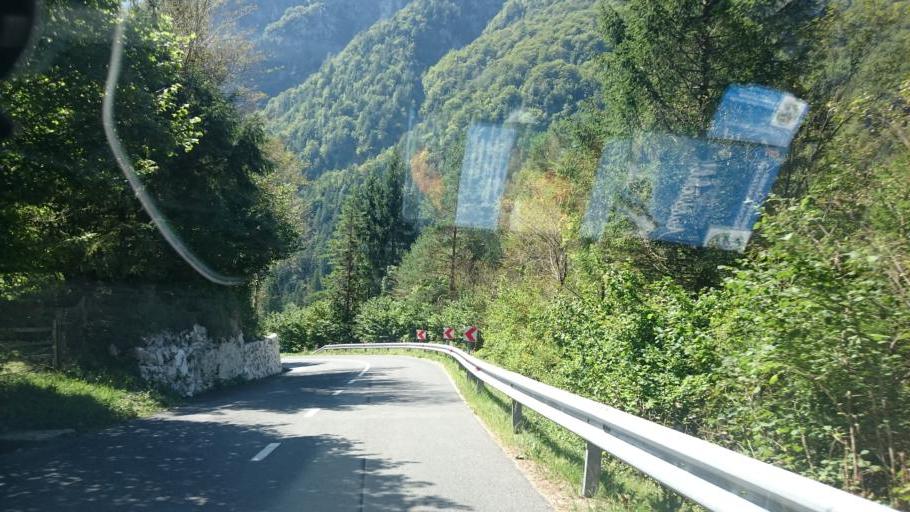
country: SI
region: Bovec
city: Bovec
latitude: 46.3776
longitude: 13.5854
